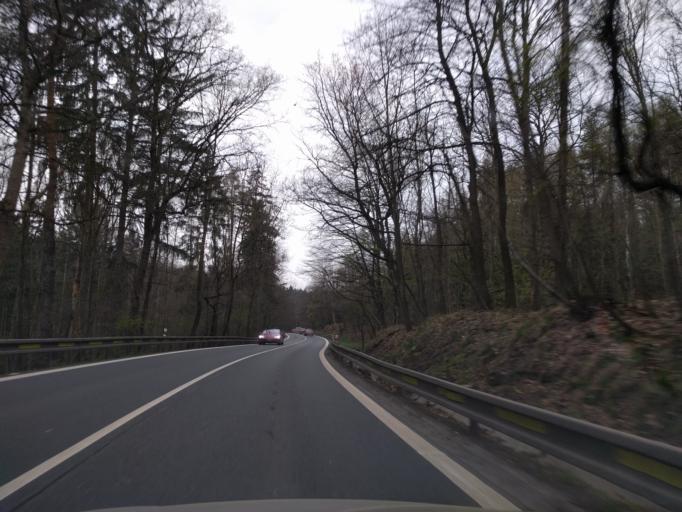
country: CZ
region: Central Bohemia
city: Mukarov
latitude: 49.9881
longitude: 14.7038
